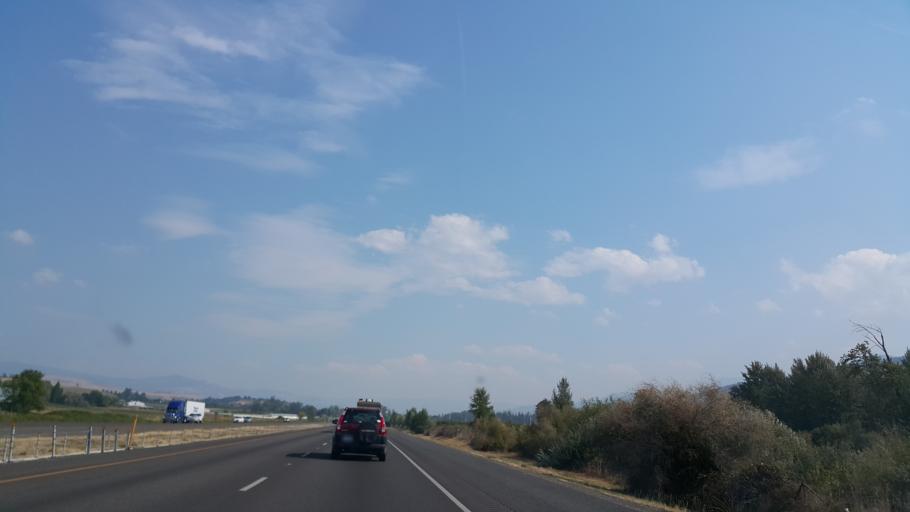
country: US
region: Oregon
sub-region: Jackson County
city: Talent
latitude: 42.2406
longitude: -122.7662
